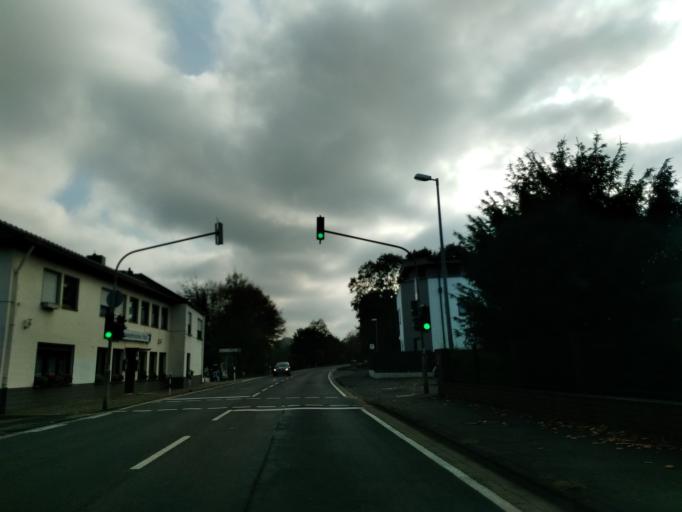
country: DE
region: North Rhine-Westphalia
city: Sankt Augustin
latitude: 50.7631
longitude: 7.2153
